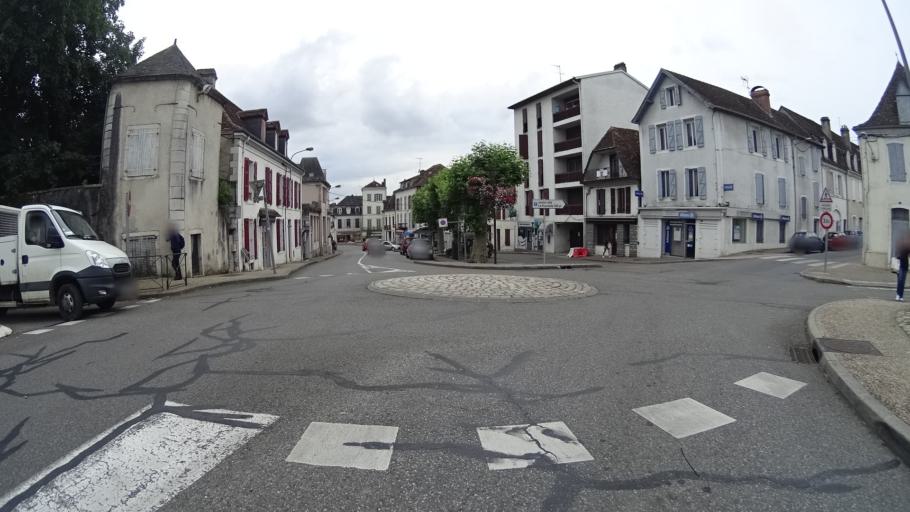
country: FR
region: Aquitaine
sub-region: Departement des Pyrenees-Atlantiques
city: Orthez
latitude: 43.4892
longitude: -0.7717
